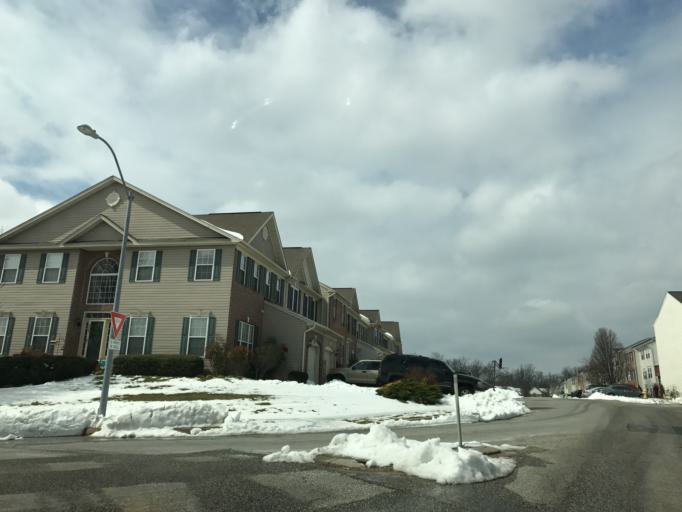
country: US
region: Maryland
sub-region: Harford County
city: Bel Air North
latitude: 39.5719
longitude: -76.3716
